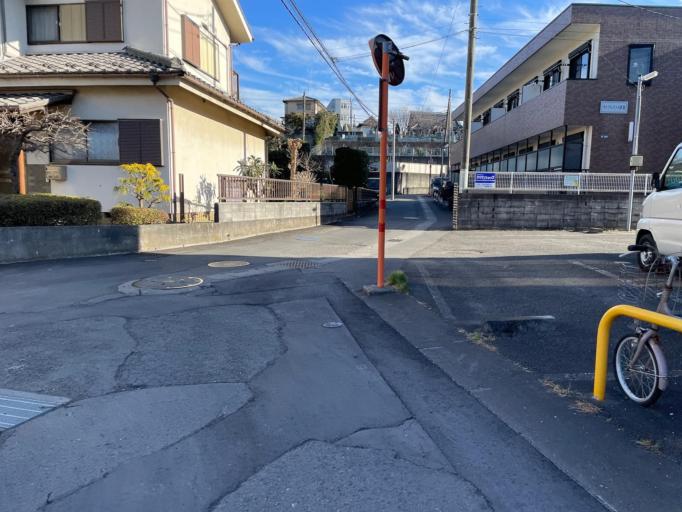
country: JP
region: Saitama
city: Sayama
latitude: 35.8356
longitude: 139.3838
